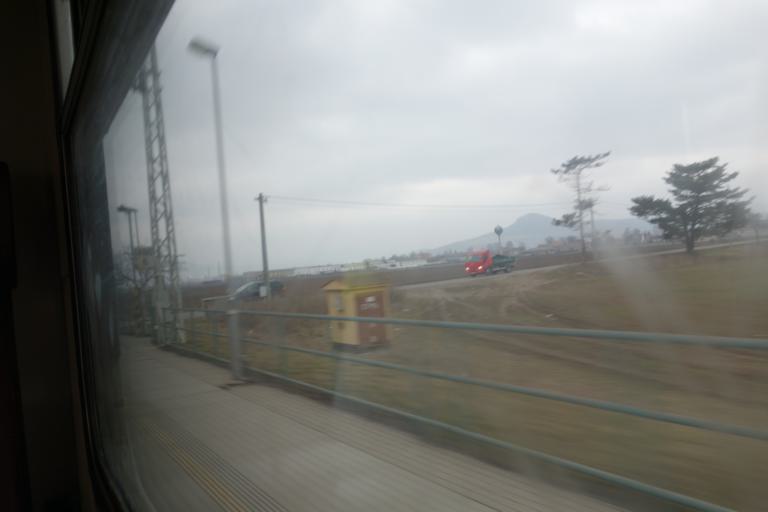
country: CZ
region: Ustecky
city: Bohusovice nad Ohri
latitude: 50.4974
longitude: 14.1201
